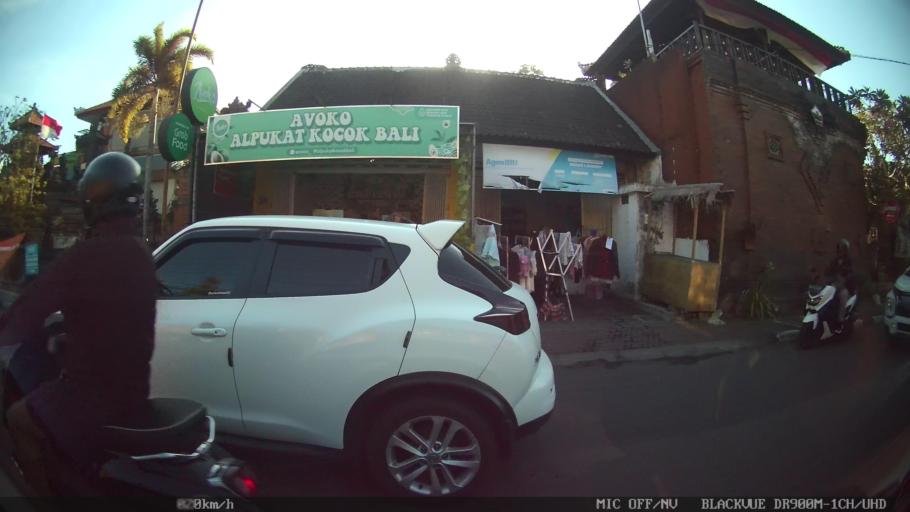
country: ID
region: Bali
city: Denpasar
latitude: -8.6488
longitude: 115.2176
